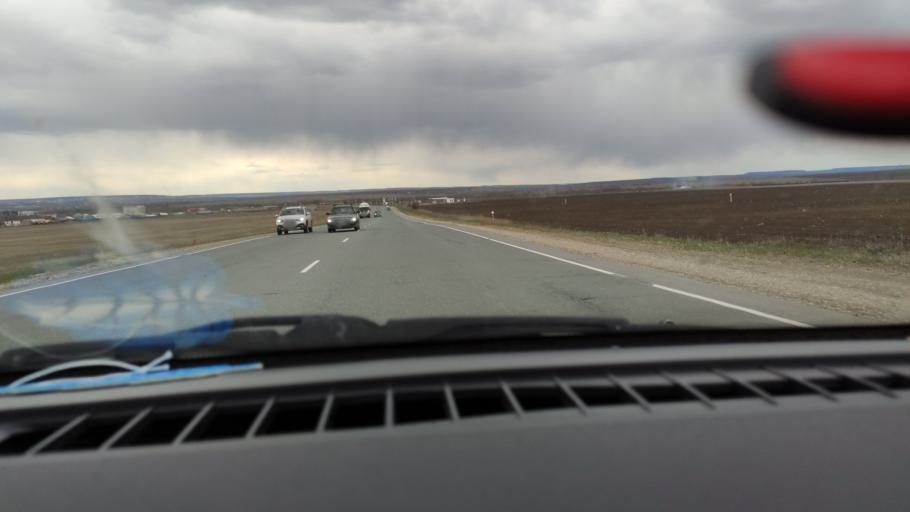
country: RU
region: Saratov
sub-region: Saratovskiy Rayon
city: Saratov
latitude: 51.7375
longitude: 46.0397
